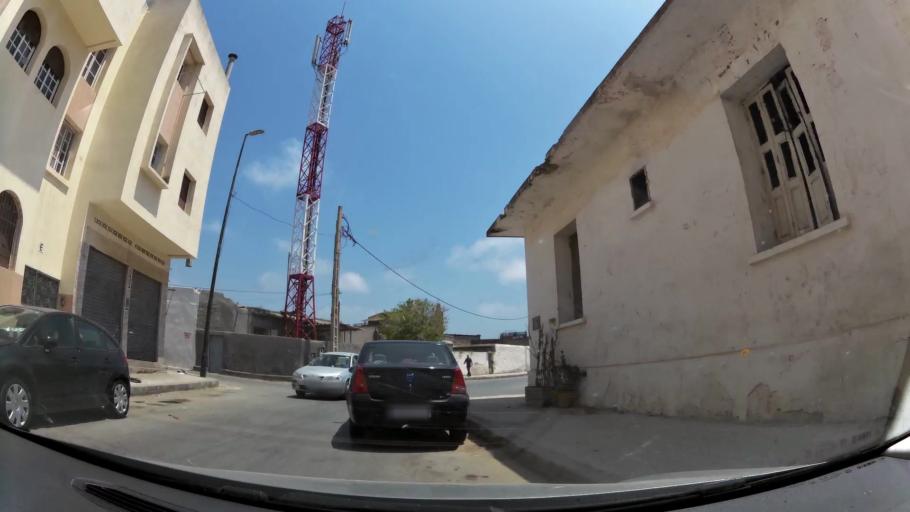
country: MA
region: Rabat-Sale-Zemmour-Zaer
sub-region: Rabat
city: Rabat
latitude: 34.0088
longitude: -6.8640
